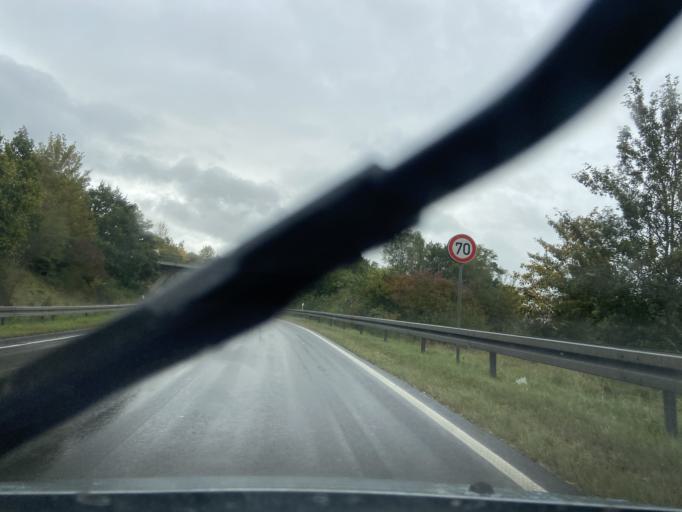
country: DE
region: Baden-Wuerttemberg
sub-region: Tuebingen Region
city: Messkirch
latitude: 48.0015
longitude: 9.1176
